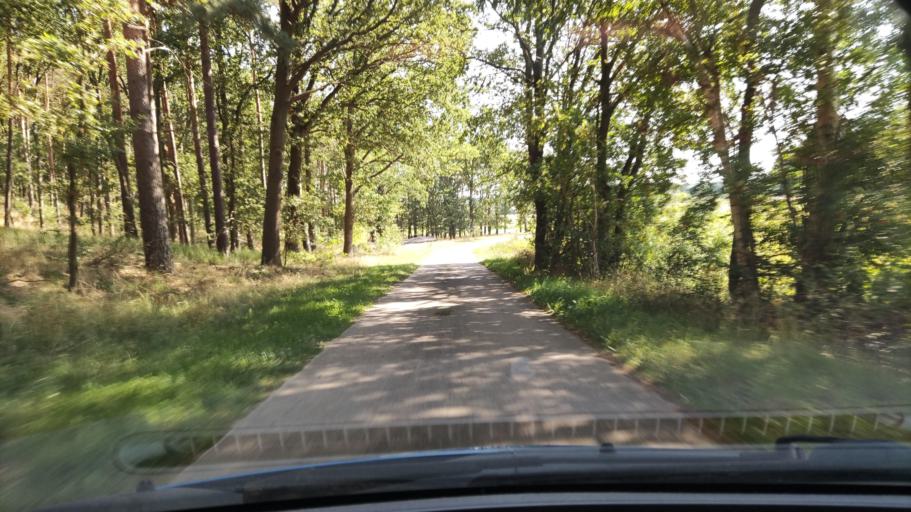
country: DE
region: Lower Saxony
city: Gohrde
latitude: 53.1411
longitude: 10.9458
